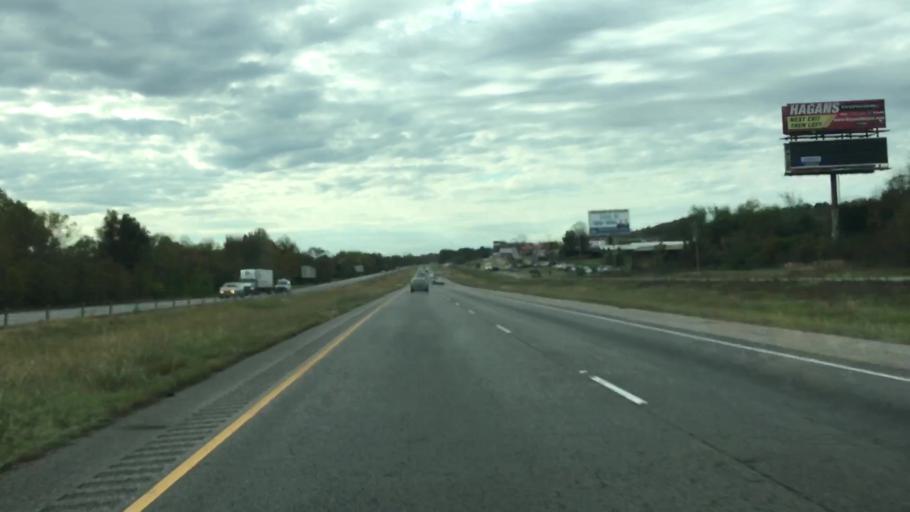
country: US
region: Arkansas
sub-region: Conway County
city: Morrilton
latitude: 35.1627
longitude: -92.6599
